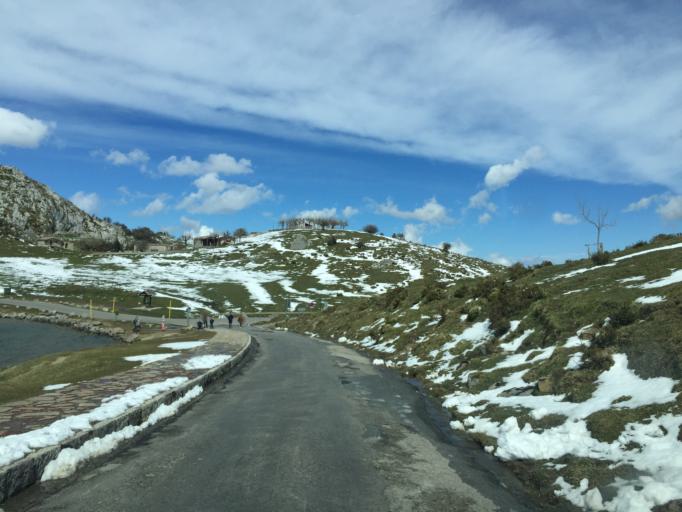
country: ES
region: Asturias
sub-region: Province of Asturias
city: Amieva
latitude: 43.2731
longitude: -4.9879
